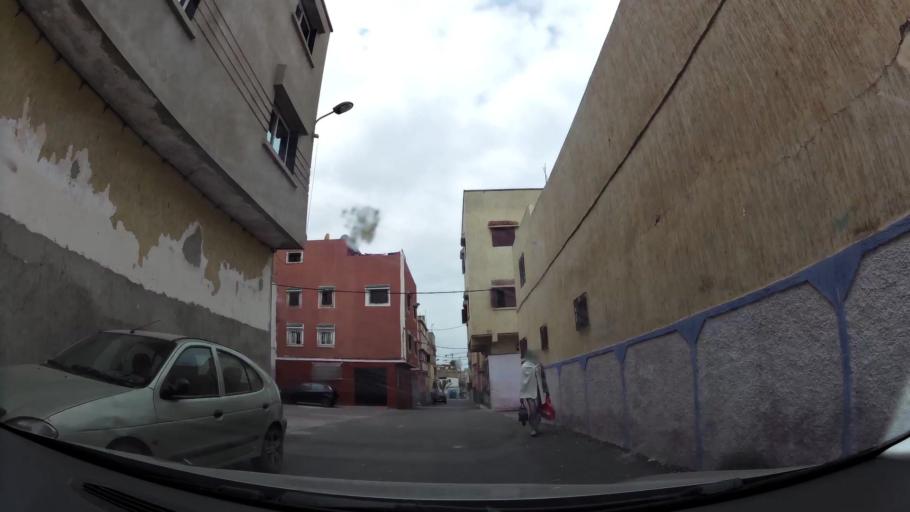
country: MA
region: Rabat-Sale-Zemmour-Zaer
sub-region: Rabat
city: Rabat
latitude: 34.0038
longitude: -6.8704
